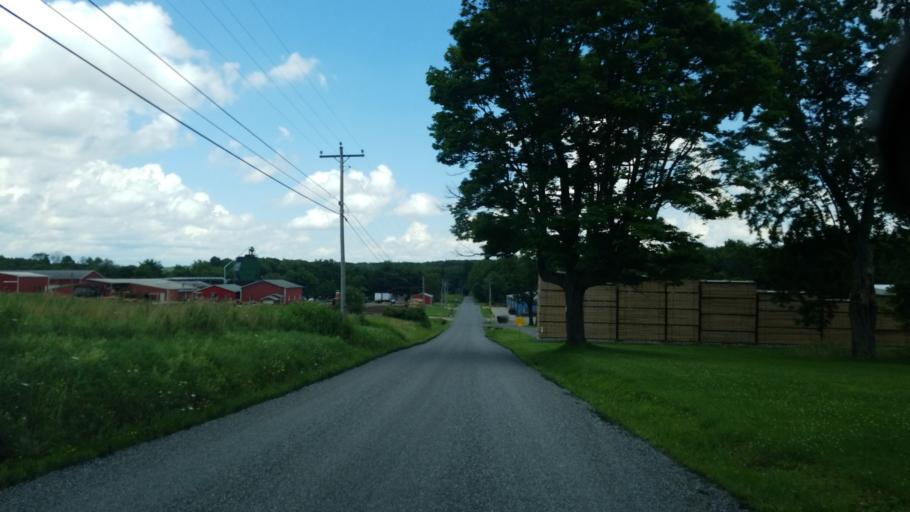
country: US
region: Pennsylvania
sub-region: Jefferson County
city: Brookville
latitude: 41.2309
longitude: -79.0014
